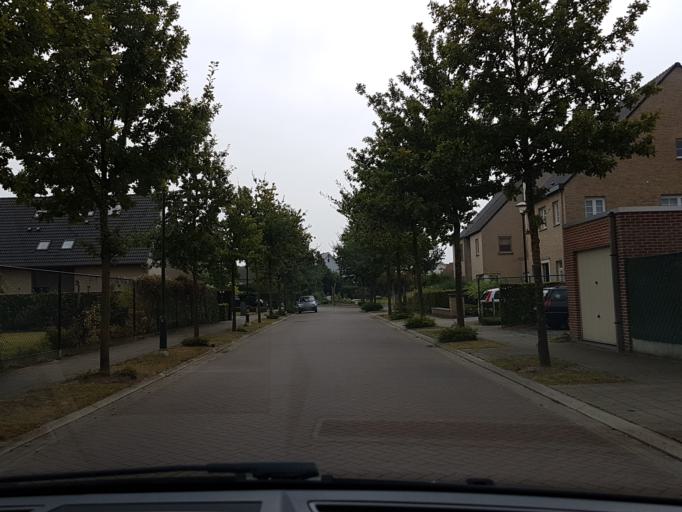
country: BE
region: Flanders
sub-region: Provincie Vlaams-Brabant
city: Machelen
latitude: 50.9164
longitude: 4.4456
